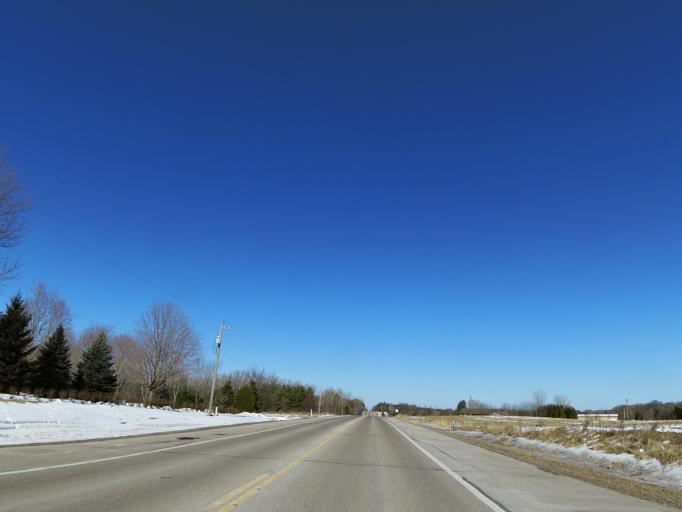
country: US
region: Minnesota
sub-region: Washington County
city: Lake Elmo
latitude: 45.0190
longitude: -92.8832
